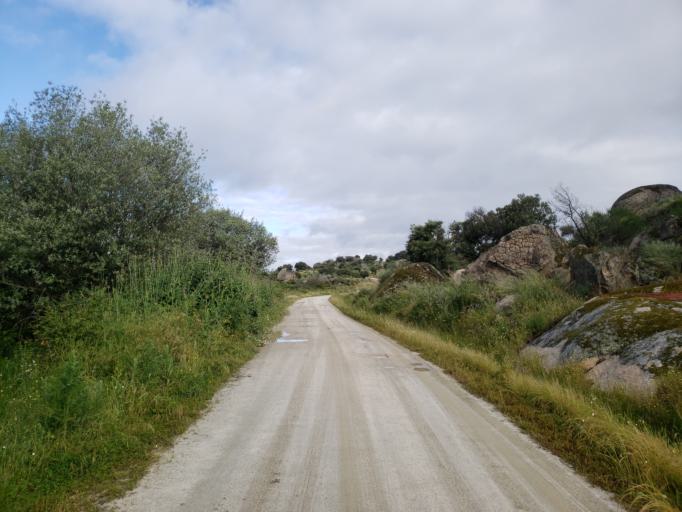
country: ES
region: Extremadura
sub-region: Provincia de Caceres
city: Malpartida de Caceres
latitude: 39.4260
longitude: -6.4918
